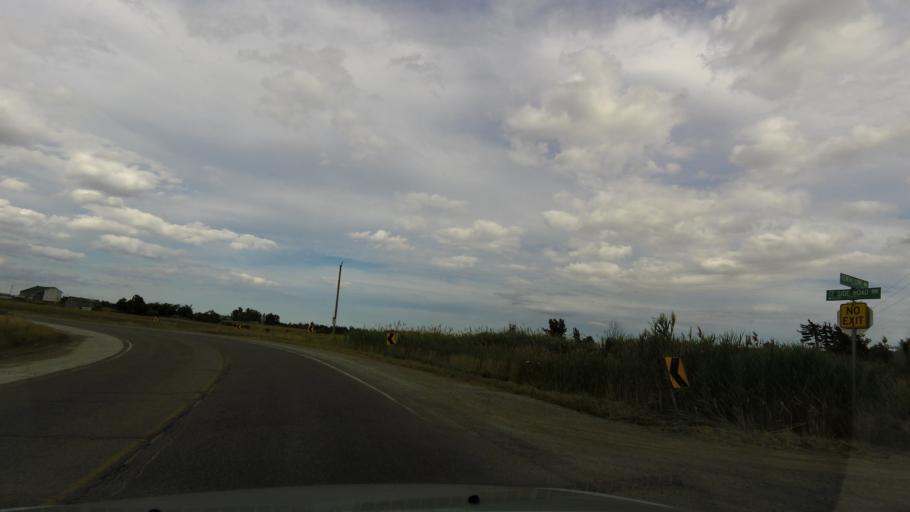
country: CA
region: Ontario
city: Brampton
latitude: 43.6656
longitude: -79.8997
